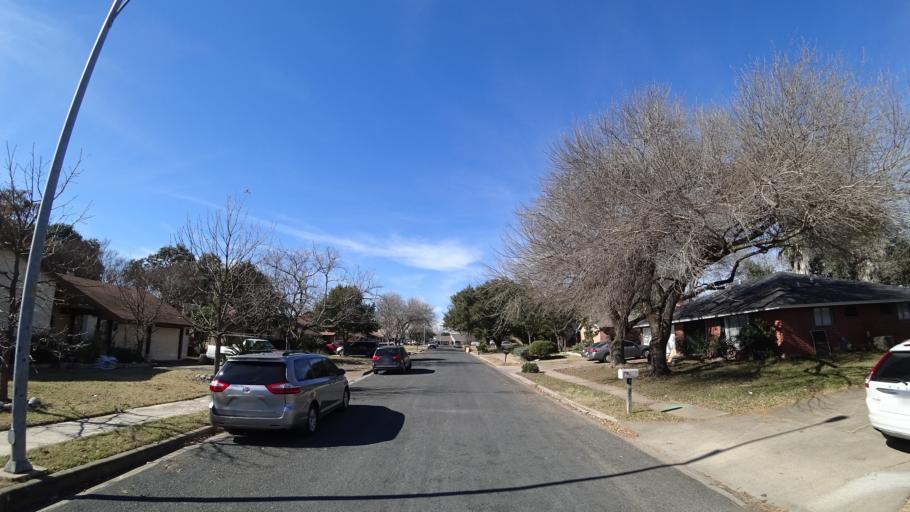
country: US
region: Texas
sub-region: Travis County
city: Wells Branch
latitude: 30.3731
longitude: -97.6989
